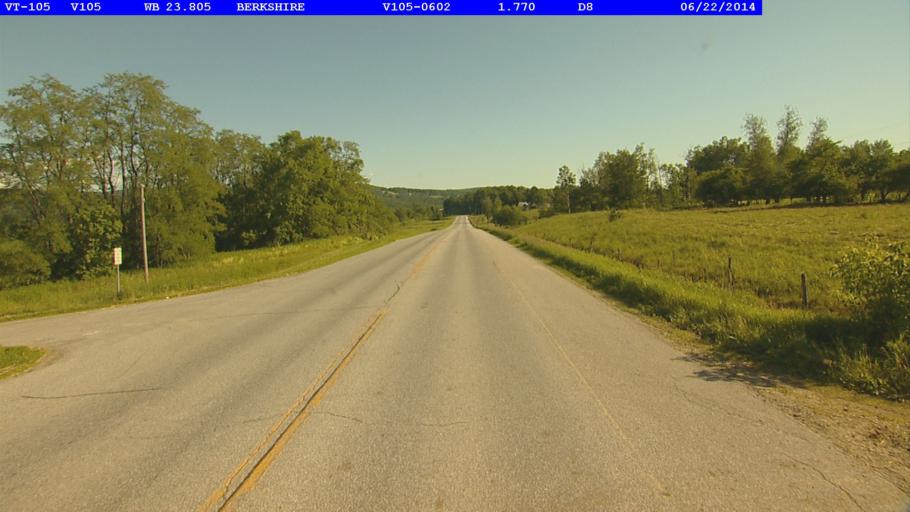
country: US
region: Vermont
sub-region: Franklin County
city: Richford
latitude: 44.9461
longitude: -72.7060
